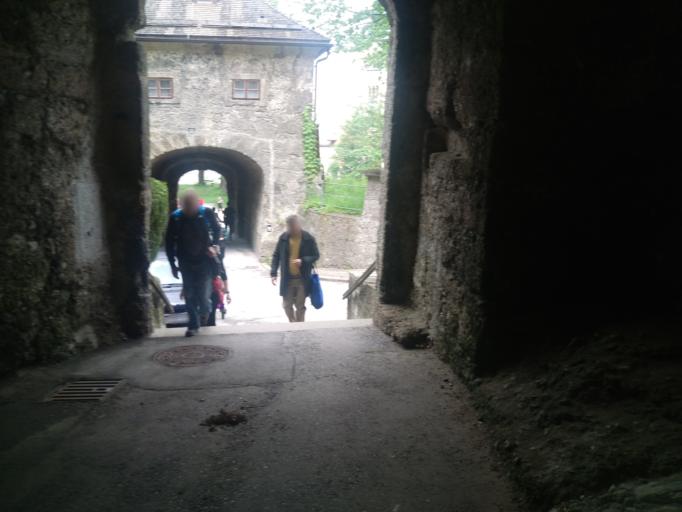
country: AT
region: Salzburg
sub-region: Salzburg Stadt
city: Salzburg
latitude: 47.8044
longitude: 13.0352
